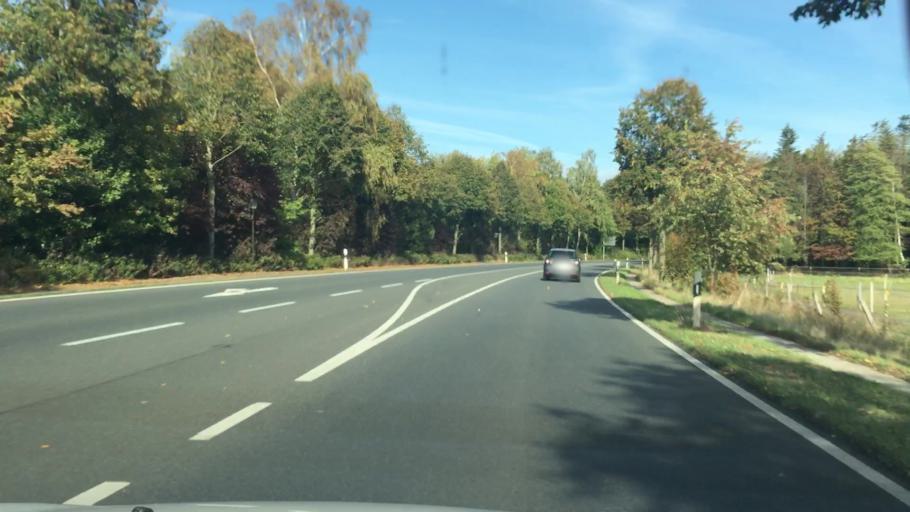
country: DE
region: Lower Saxony
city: Wehrbleck
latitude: 52.6320
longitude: 8.6913
